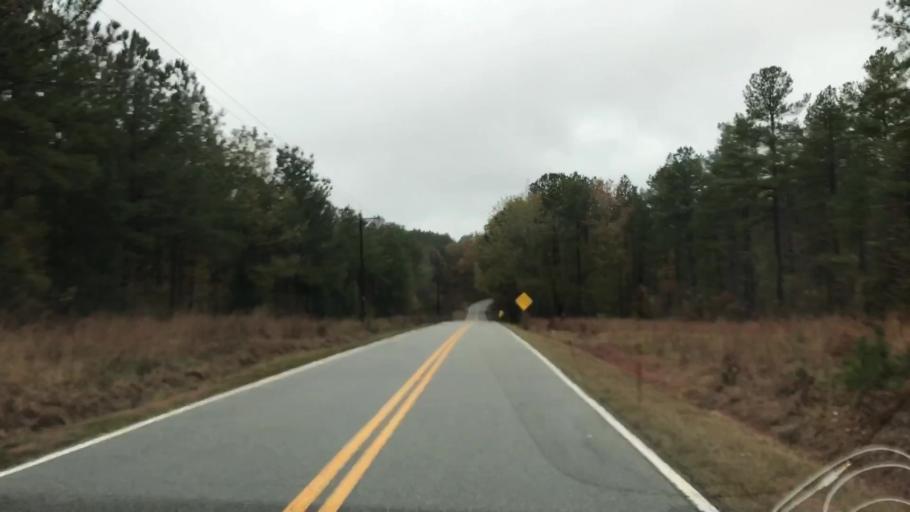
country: US
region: South Carolina
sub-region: Greenwood County
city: Ninety Six
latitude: 34.3119
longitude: -81.9441
